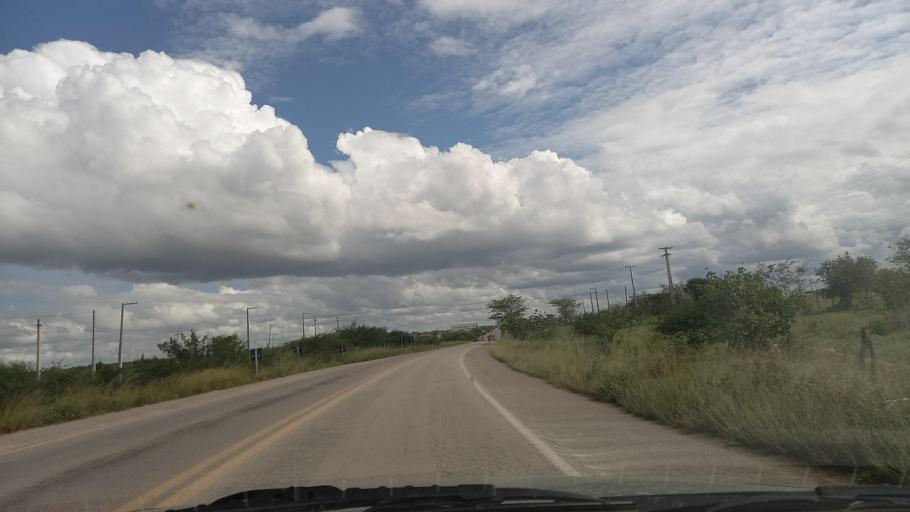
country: BR
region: Pernambuco
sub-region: Cachoeirinha
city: Cachoeirinha
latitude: -8.4838
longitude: -36.2260
